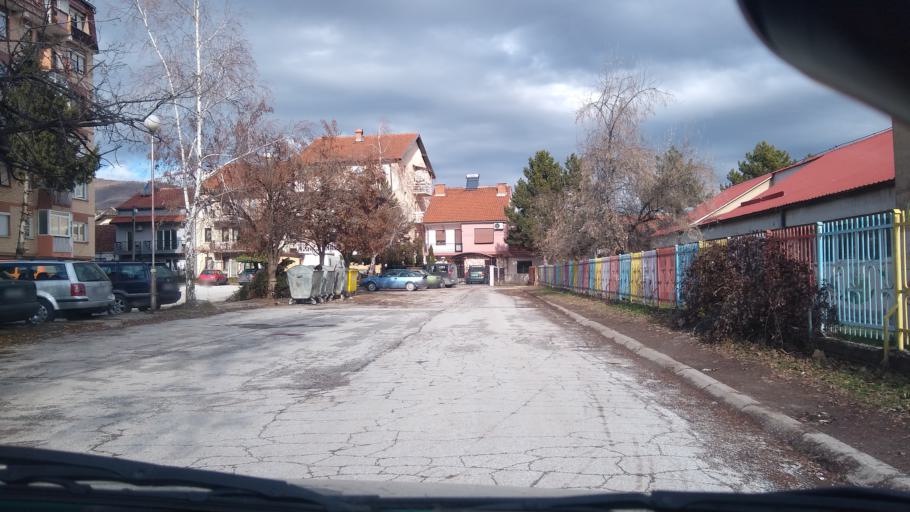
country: MK
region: Bitola
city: Bitola
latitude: 41.0266
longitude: 21.3185
